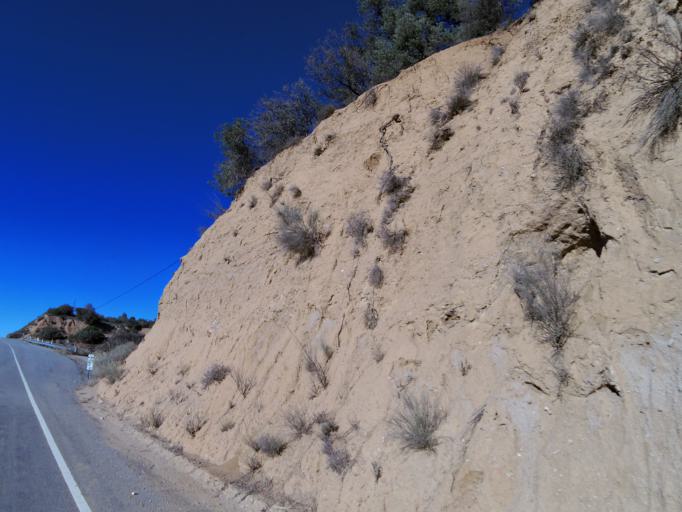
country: US
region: California
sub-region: Kern County
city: Pine Mountain Club
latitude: 34.7693
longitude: -119.4217
